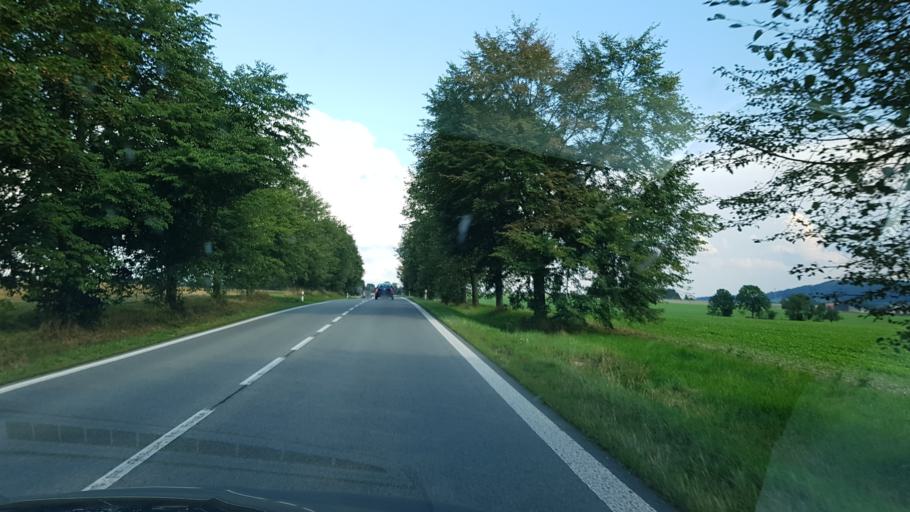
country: CZ
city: Vamberk
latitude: 50.1076
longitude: 16.3695
